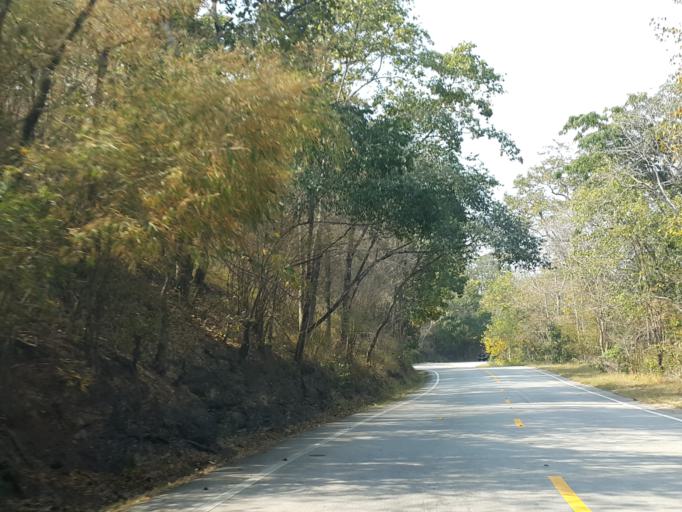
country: TH
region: Chiang Mai
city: Hot
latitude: 18.2303
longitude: 98.5187
